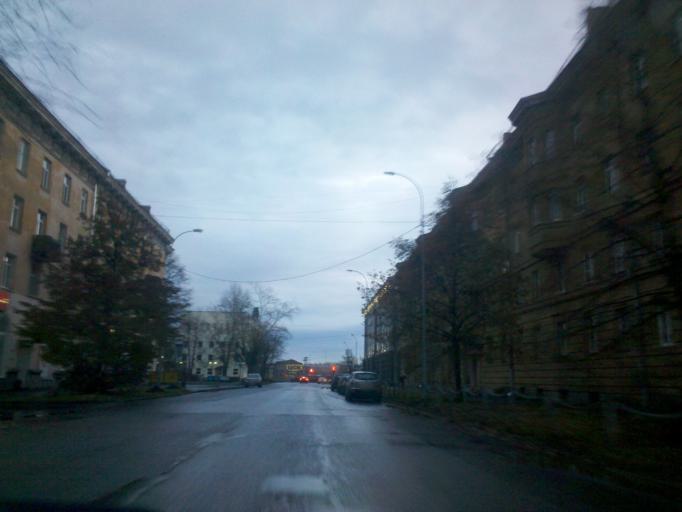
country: RU
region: Republic of Karelia
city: Petrozavodsk
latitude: 61.7896
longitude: 34.3730
